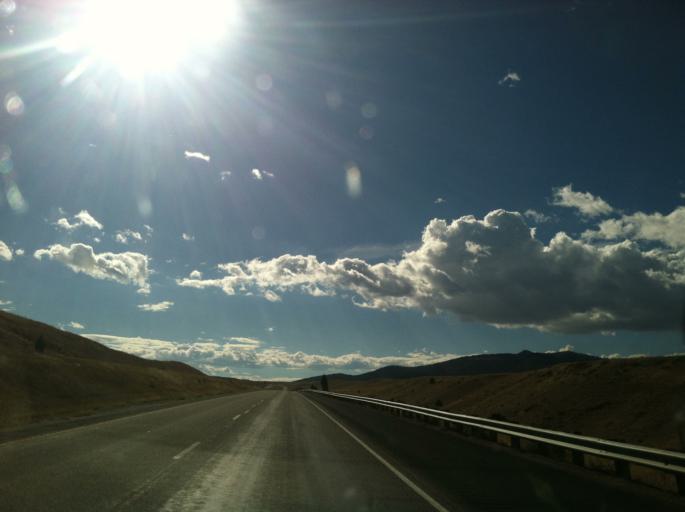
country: US
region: Montana
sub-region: Jefferson County
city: Whitehall
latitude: 45.8983
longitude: -111.8267
